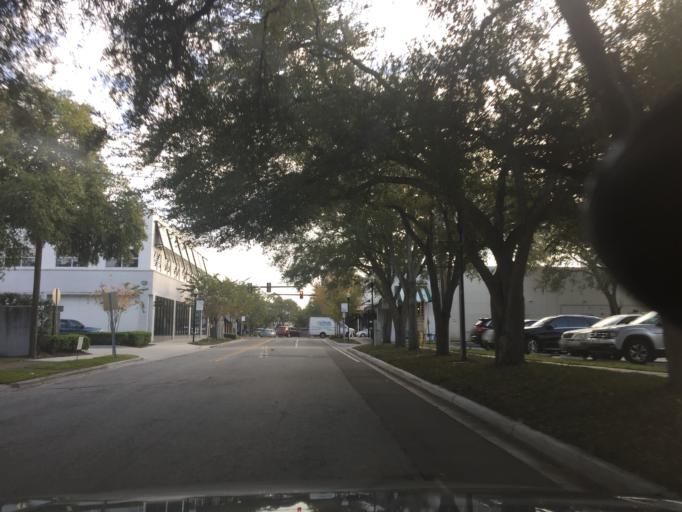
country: US
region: Florida
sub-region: Hillsborough County
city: Tampa
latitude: 27.9381
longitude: -82.4758
